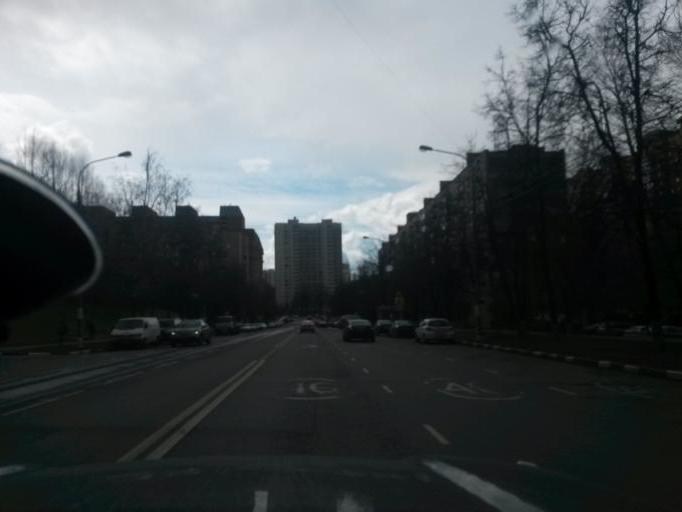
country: RU
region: Moskovskaya
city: Semenovskoye
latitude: 55.6779
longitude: 37.5431
